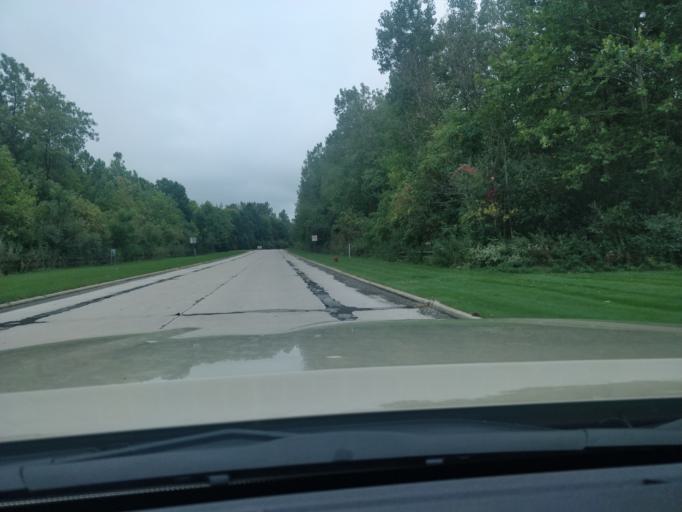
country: US
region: Michigan
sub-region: Wayne County
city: Romulus
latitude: 42.1728
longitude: -83.3919
